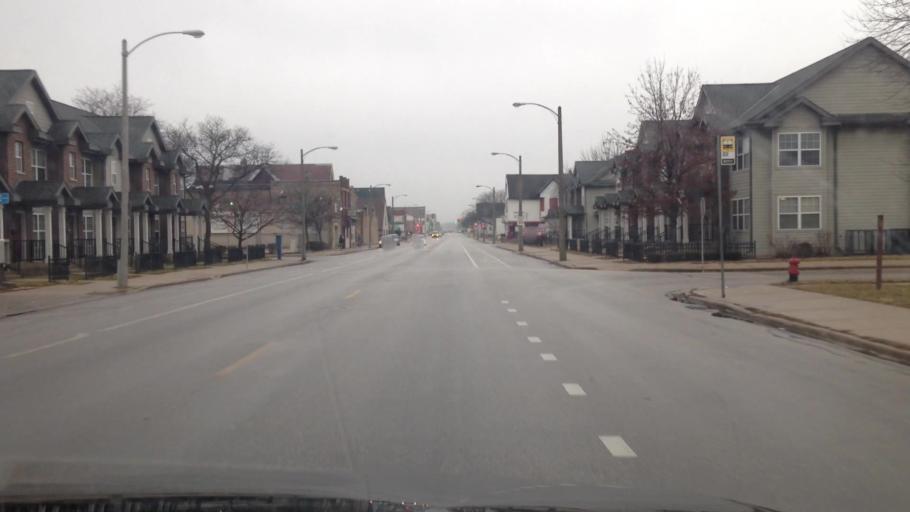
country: US
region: Wisconsin
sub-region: Milwaukee County
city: Milwaukee
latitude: 43.0678
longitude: -87.9341
